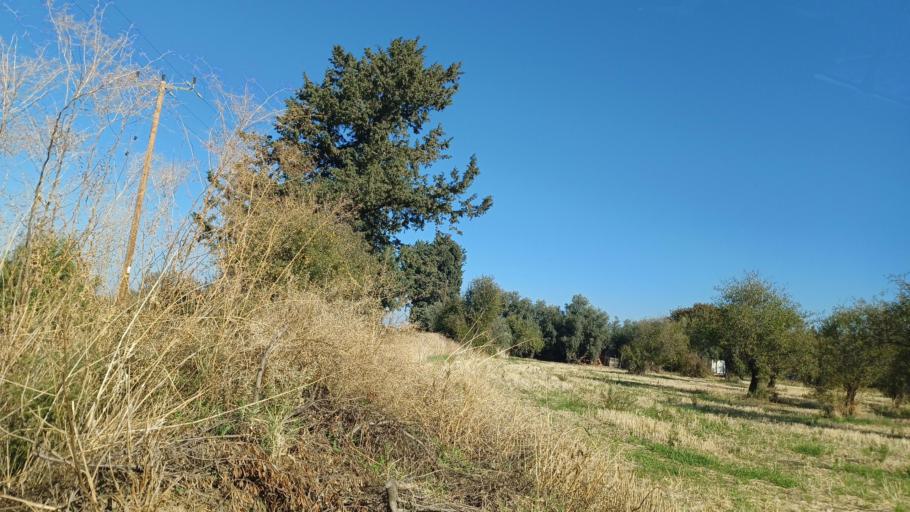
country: CY
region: Pafos
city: Polis
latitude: 35.0187
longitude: 32.4316
